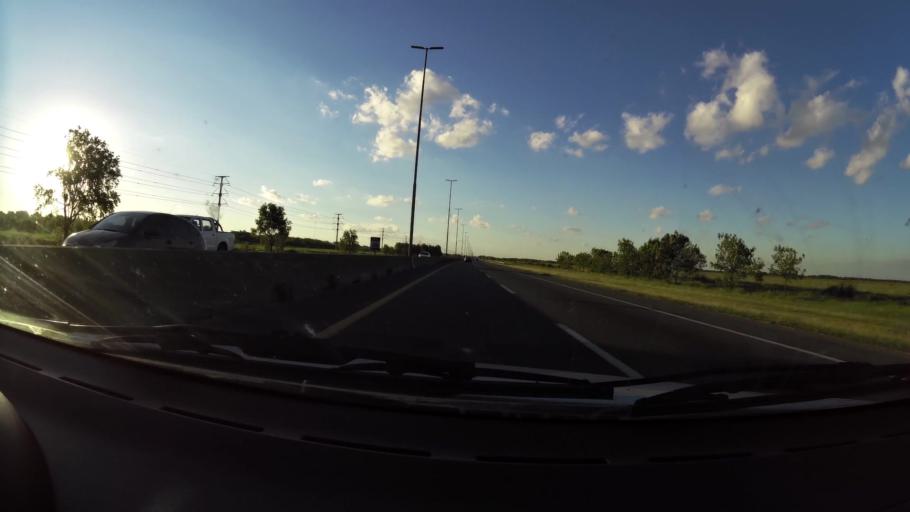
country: AR
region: Buenos Aires
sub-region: Partido de La Plata
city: La Plata
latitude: -34.8282
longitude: -58.0926
